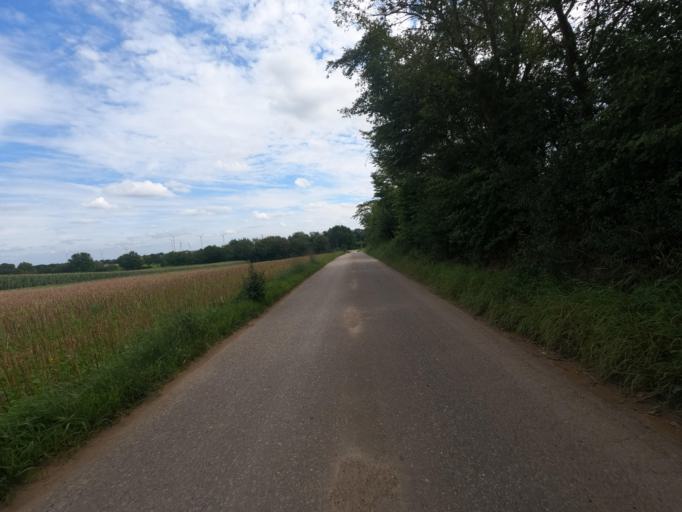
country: DE
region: North Rhine-Westphalia
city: Geilenkirchen
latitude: 50.9852
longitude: 6.1717
